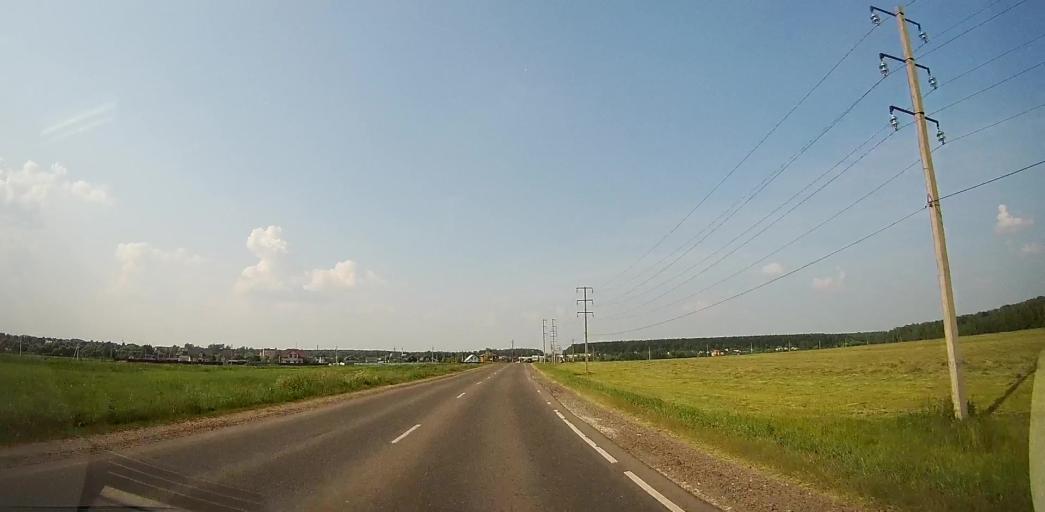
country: RU
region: Moskovskaya
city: Barybino
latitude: 55.2687
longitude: 37.9156
